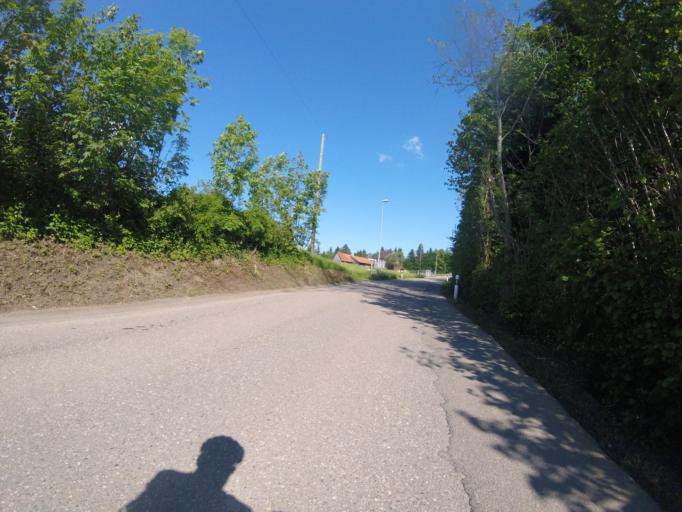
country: CH
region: Saint Gallen
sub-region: Wahlkreis Wil
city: Degersheim
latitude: 47.4024
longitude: 9.2138
